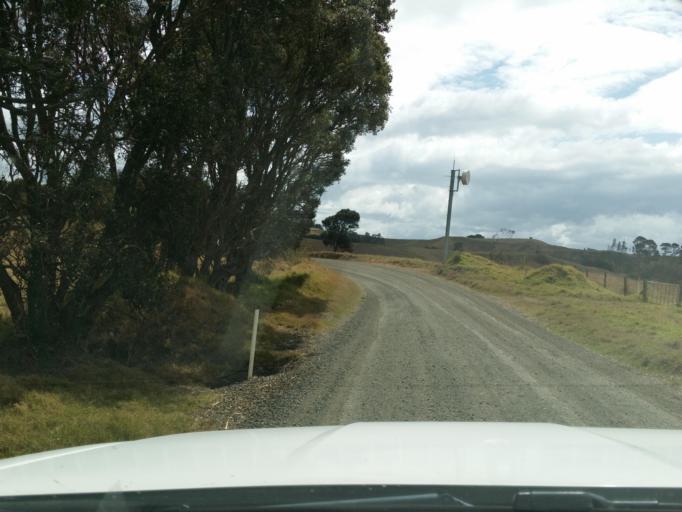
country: NZ
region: Auckland
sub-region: Auckland
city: Wellsford
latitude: -36.3366
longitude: 174.1587
